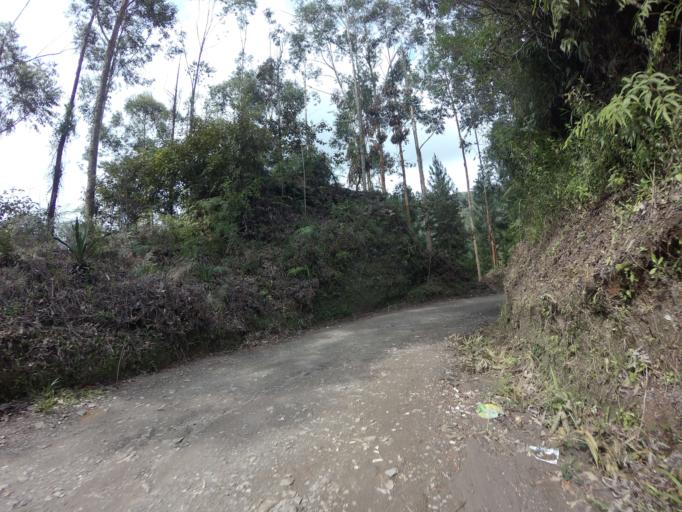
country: CO
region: Caldas
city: Marquetalia
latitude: 5.3015
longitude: -75.0434
